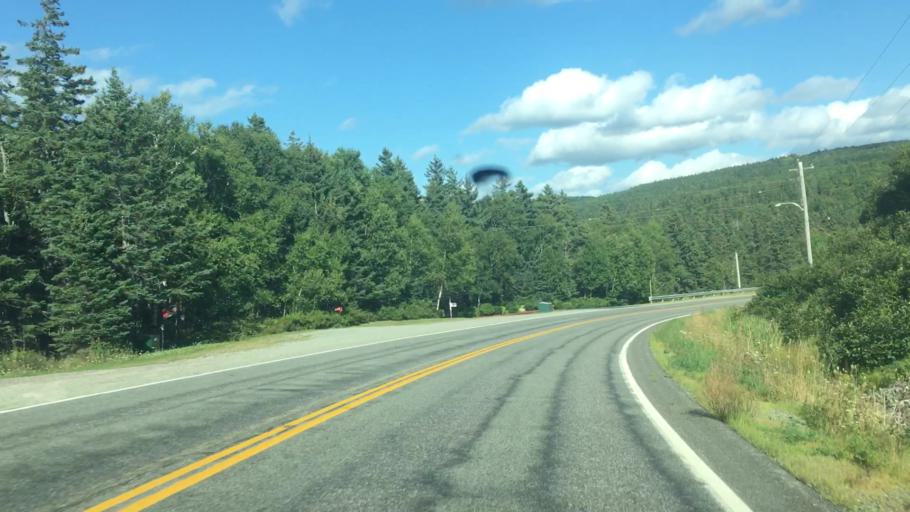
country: CA
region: Nova Scotia
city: Sydney
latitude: 45.8673
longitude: -60.6187
